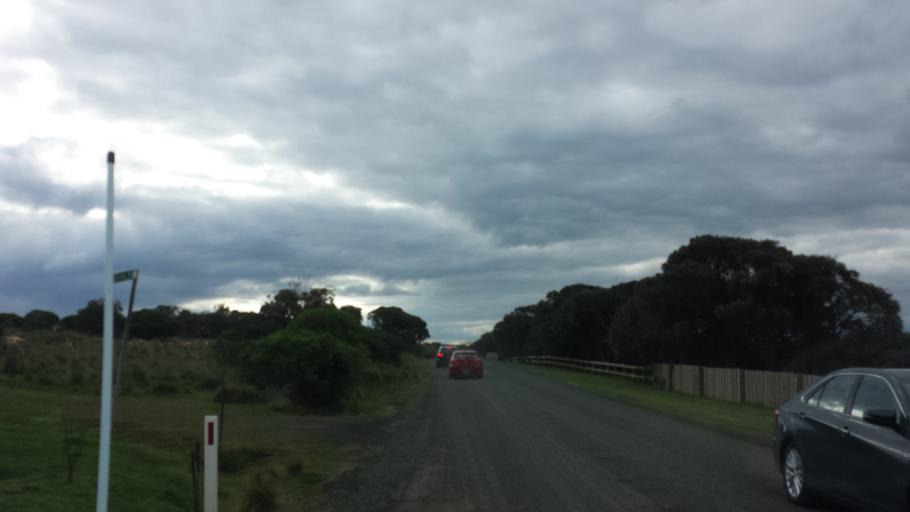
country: AU
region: Victoria
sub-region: Bass Coast
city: Phillip Island
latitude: -38.5087
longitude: 145.1470
